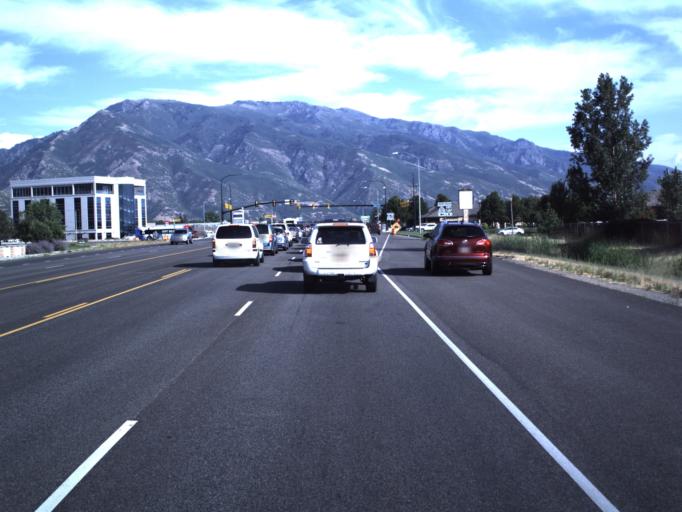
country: US
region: Utah
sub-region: Weber County
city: Uintah
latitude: 41.1569
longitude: -111.9423
